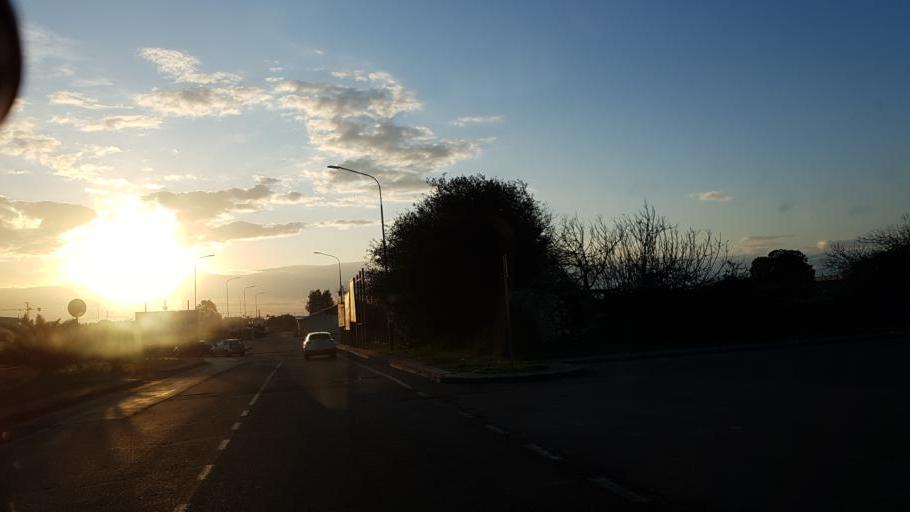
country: IT
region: Apulia
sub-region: Provincia di Lecce
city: Giorgilorio
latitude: 40.3814
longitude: 18.1399
